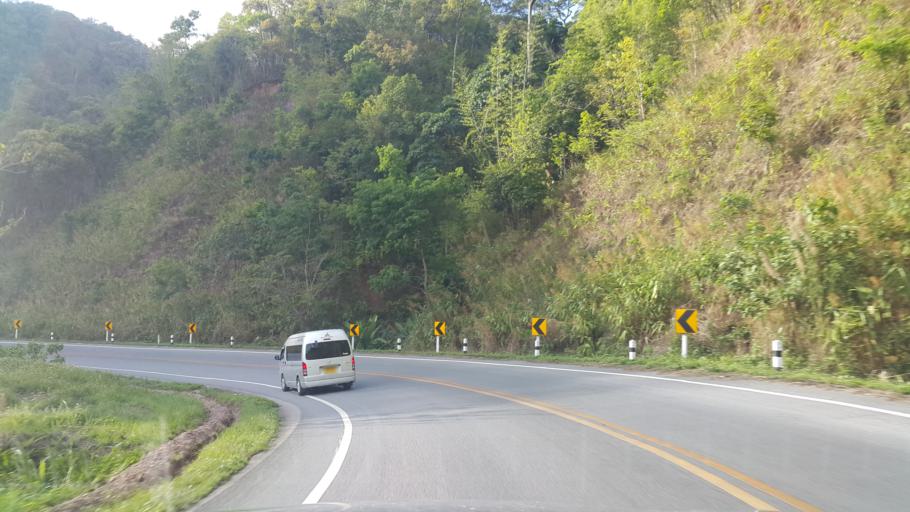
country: TH
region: Phayao
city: Phayao
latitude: 19.0725
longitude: 99.7726
